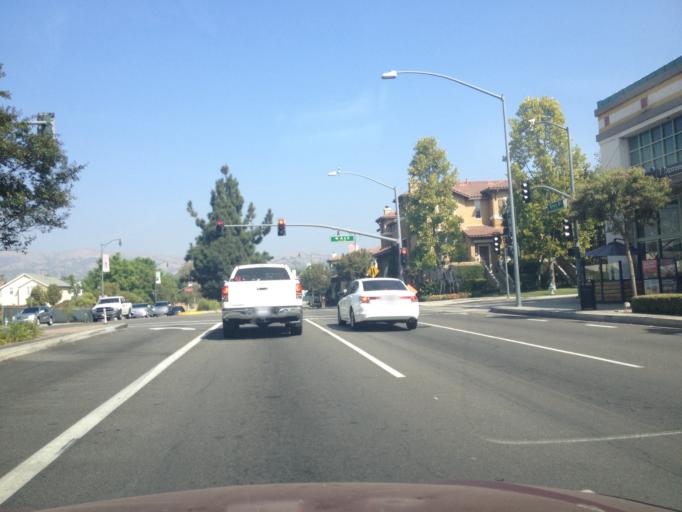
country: US
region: California
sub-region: Orange County
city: Brea
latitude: 33.9195
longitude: -117.8986
